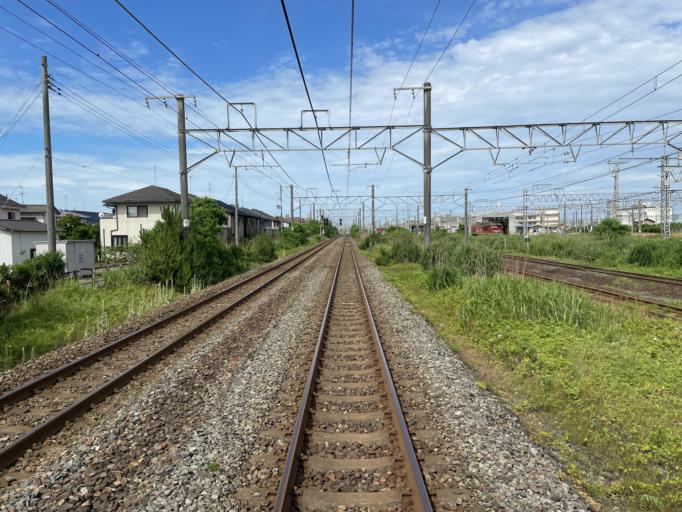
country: JP
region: Niigata
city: Kameda-honcho
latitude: 37.9124
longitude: 139.1181
